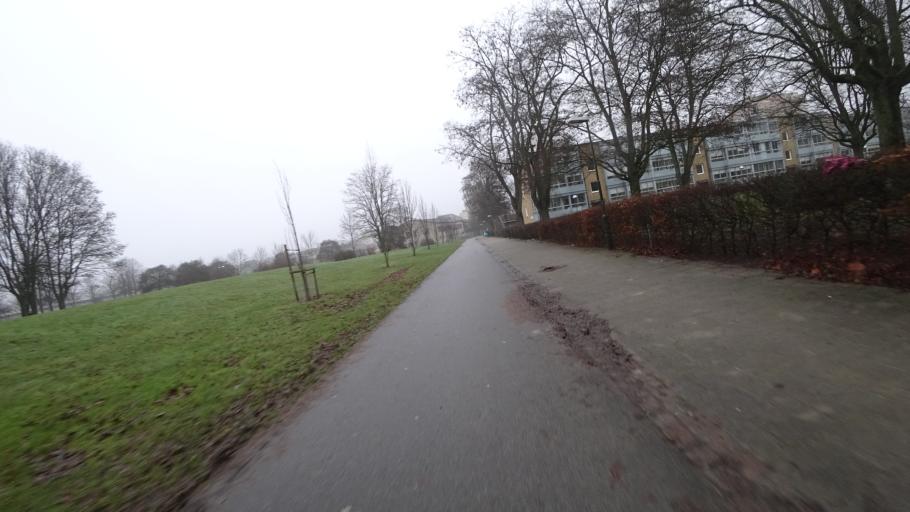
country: SE
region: Skane
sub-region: Malmo
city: Malmoe
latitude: 55.5823
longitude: 12.9939
